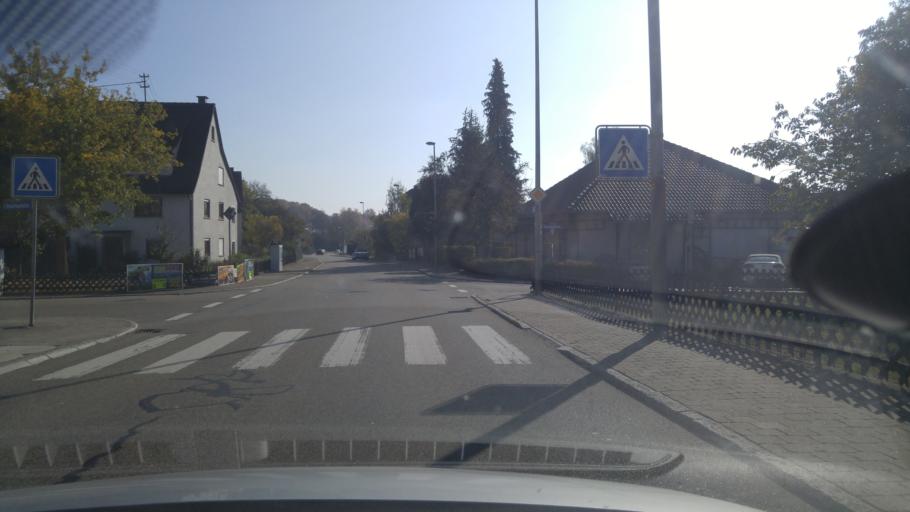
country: DE
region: Baden-Wuerttemberg
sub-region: Karlsruhe Region
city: Empfingen
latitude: 48.3918
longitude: 8.7133
